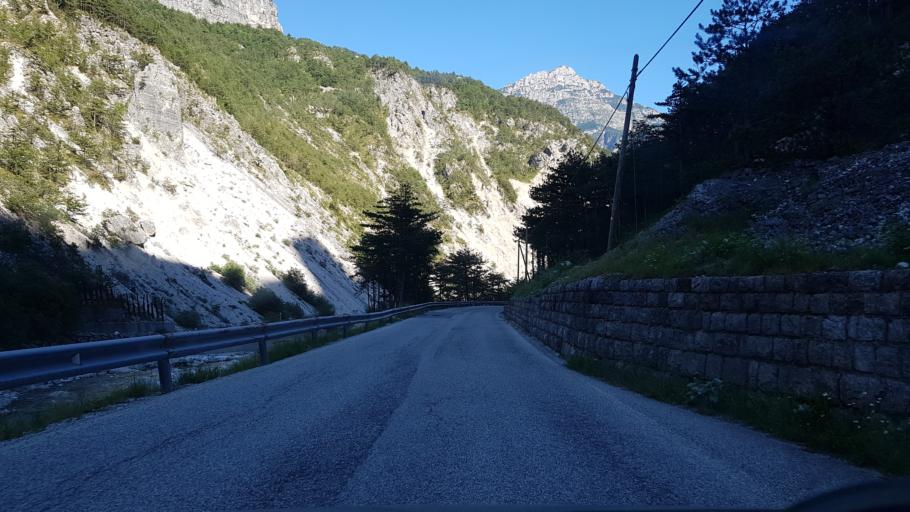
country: IT
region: Friuli Venezia Giulia
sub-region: Provincia di Udine
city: Moggio Udinese
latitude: 46.4439
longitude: 13.1919
